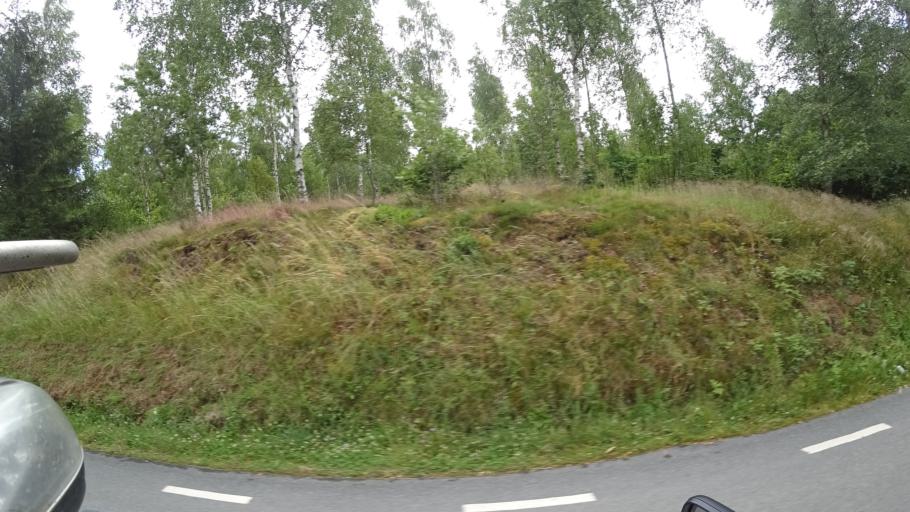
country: SE
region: Skane
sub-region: Kristianstads Kommun
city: Degeberga
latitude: 55.7177
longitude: 13.9899
